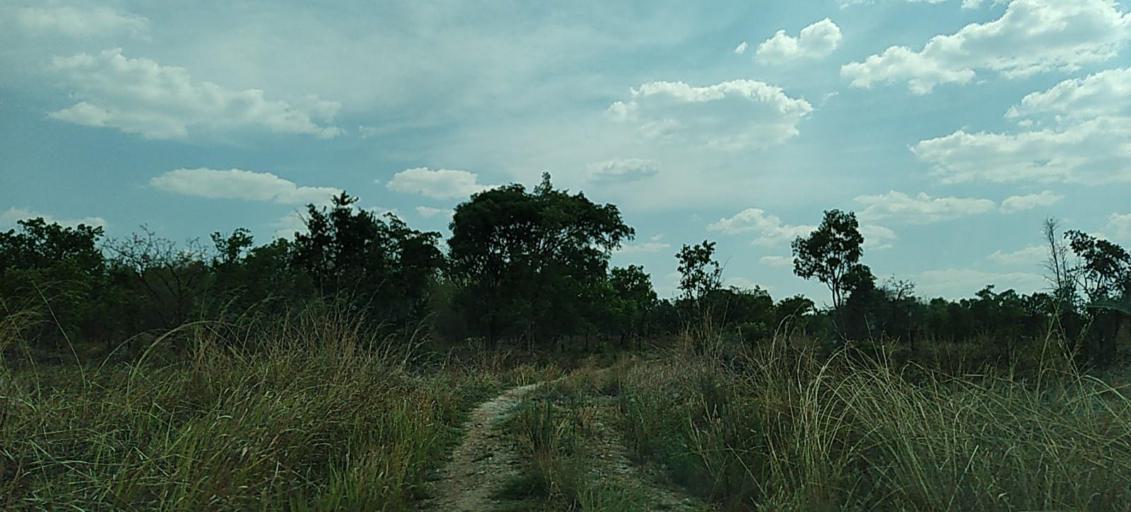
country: ZM
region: Copperbelt
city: Chililabombwe
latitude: -12.3354
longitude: 27.7830
